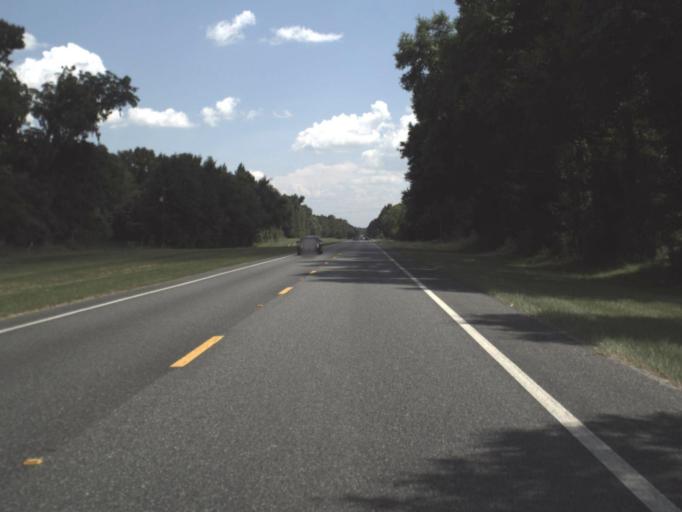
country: US
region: Florida
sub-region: Alachua County
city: High Springs
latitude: 29.8712
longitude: -82.6088
